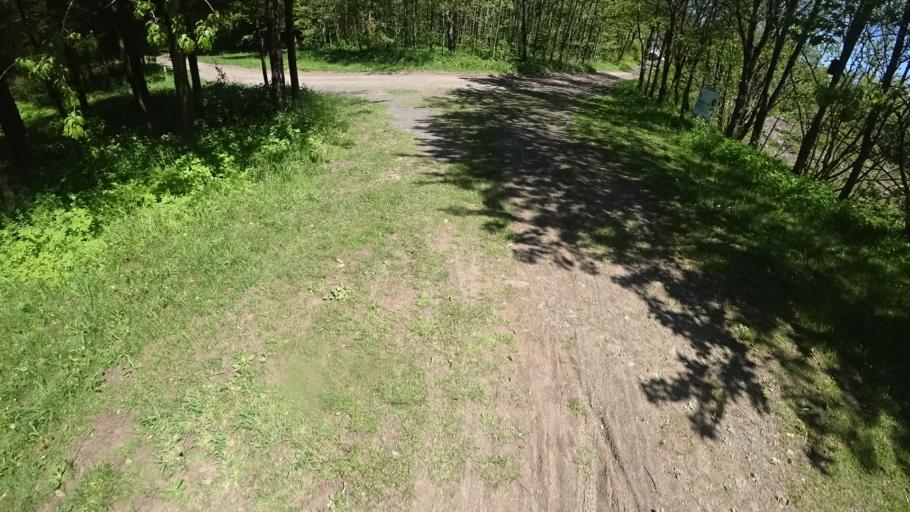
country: DE
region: Rheinland-Pfalz
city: Steineroth
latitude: 50.7531
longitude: 7.8459
